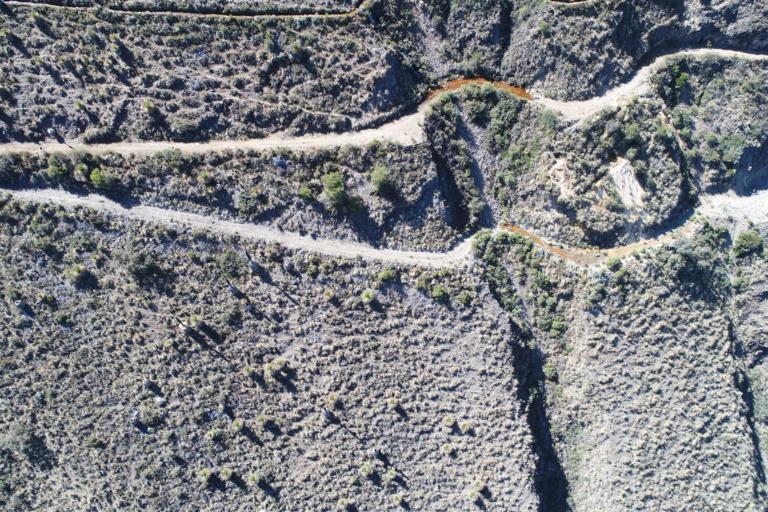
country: BO
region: La Paz
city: Viloco
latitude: -16.8095
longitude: -67.5536
